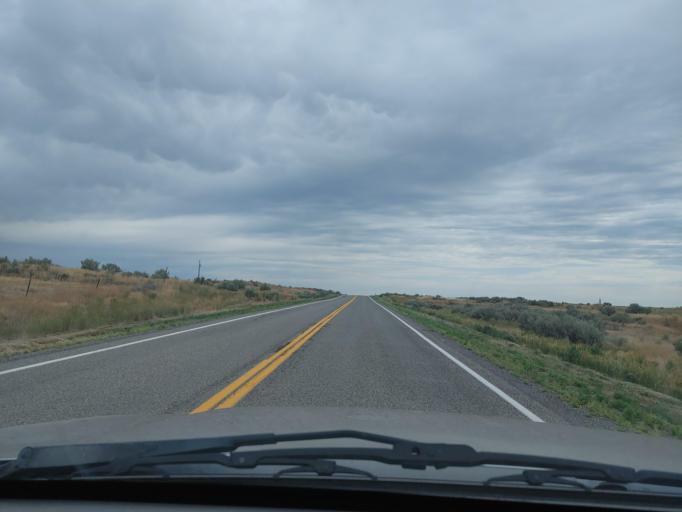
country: US
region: Idaho
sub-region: Lincoln County
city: Shoshone
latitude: 43.0558
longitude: -114.1344
